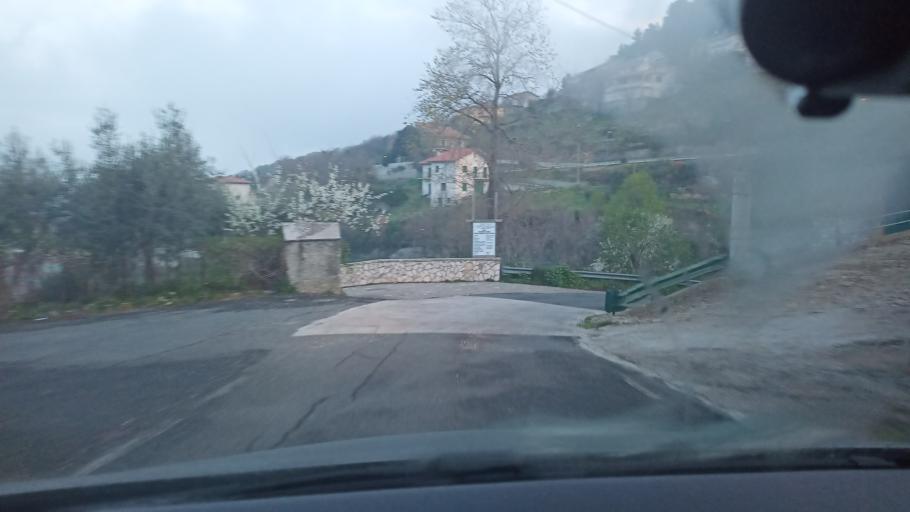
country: IT
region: Latium
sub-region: Provincia di Rieti
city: Cottanello
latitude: 42.4078
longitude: 12.6864
